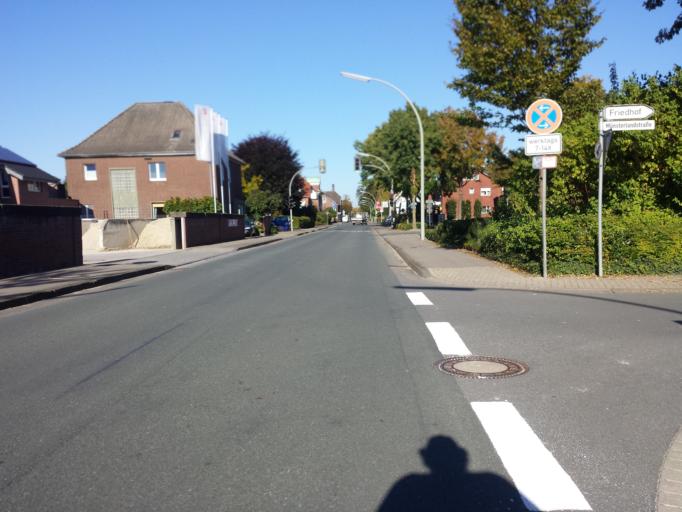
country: DE
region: North Rhine-Westphalia
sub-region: Regierungsbezirk Detmold
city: Langenberg
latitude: 51.7472
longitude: 8.3245
